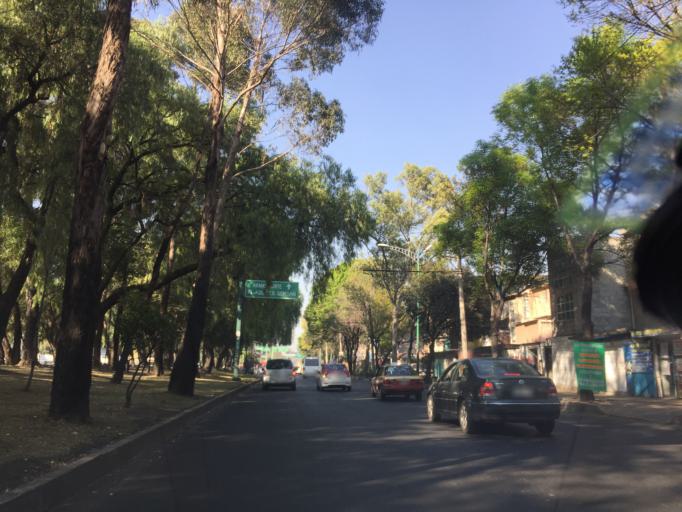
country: MX
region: Mexico
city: Vista Hermosa
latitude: 19.5088
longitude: -99.2068
